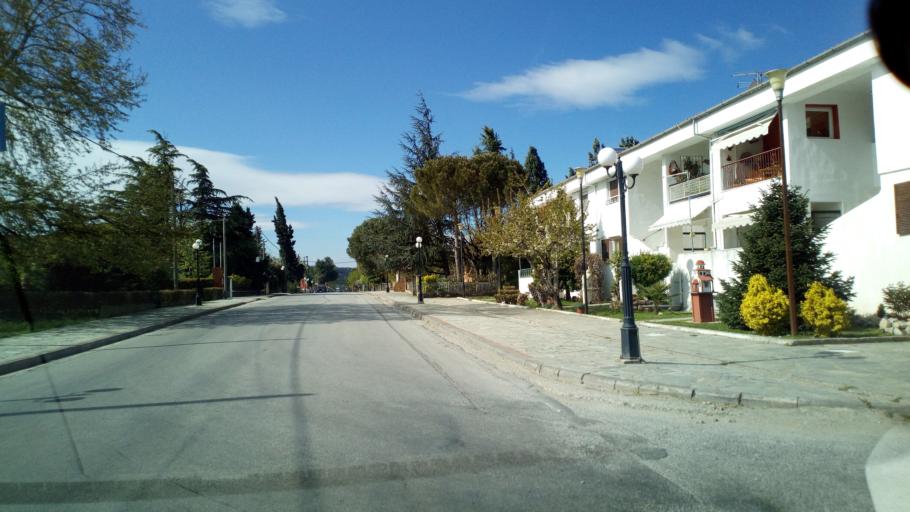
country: GR
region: Central Macedonia
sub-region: Nomos Kilkis
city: Nea Santa
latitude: 40.8342
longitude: 22.8951
